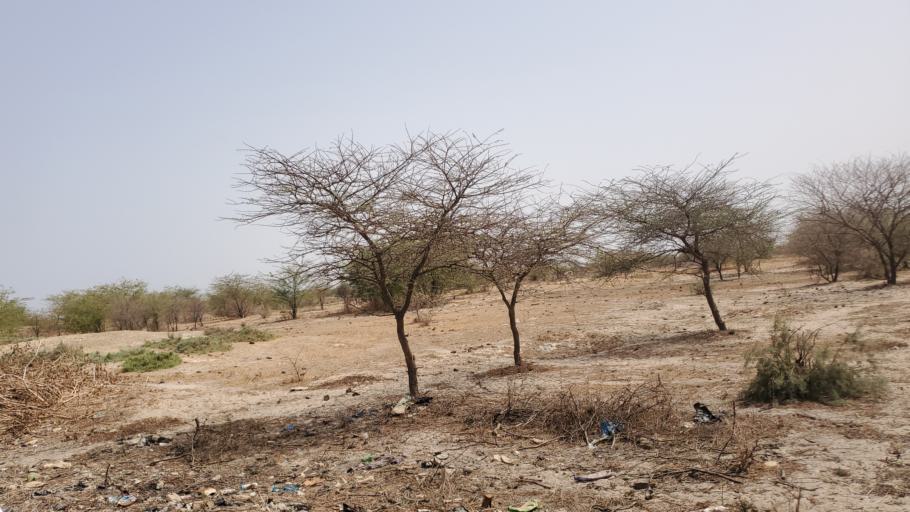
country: SN
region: Saint-Louis
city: Saint-Louis
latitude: 15.9504
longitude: -16.4310
